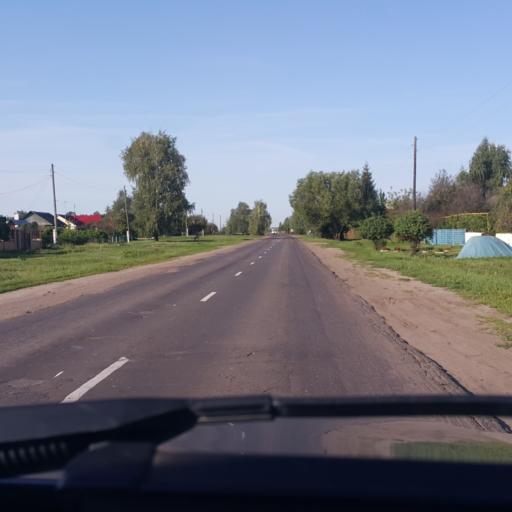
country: RU
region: Tambov
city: Novaya Lyada
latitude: 52.7724
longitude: 41.7490
